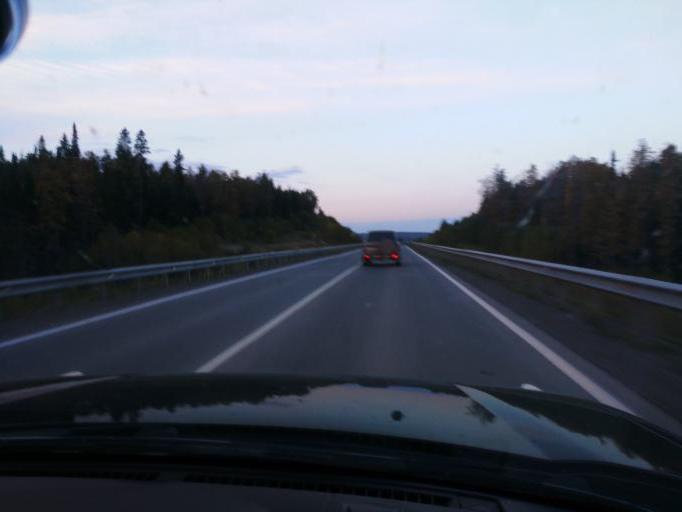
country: RU
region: Perm
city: Sylva
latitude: 58.2899
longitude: 56.7469
